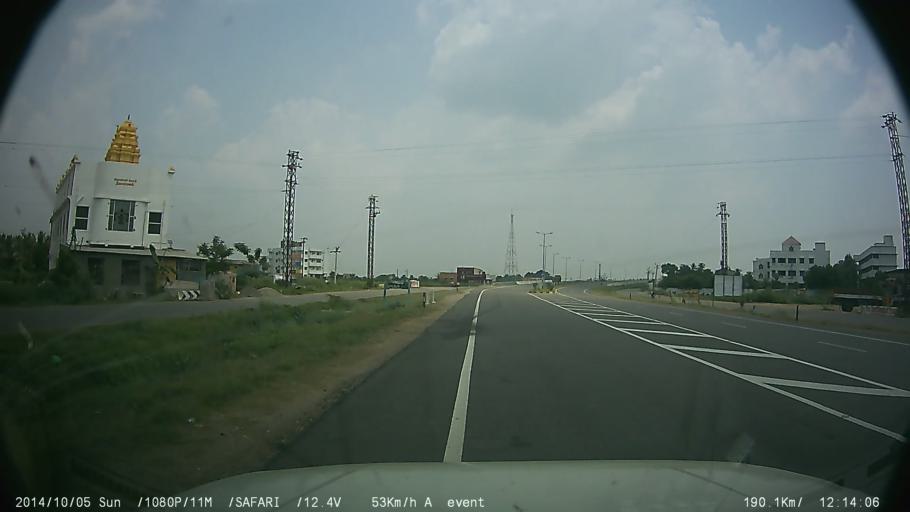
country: IN
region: Tamil Nadu
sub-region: Villupuram
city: Kallakkurichchi
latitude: 11.7370
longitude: 78.9886
